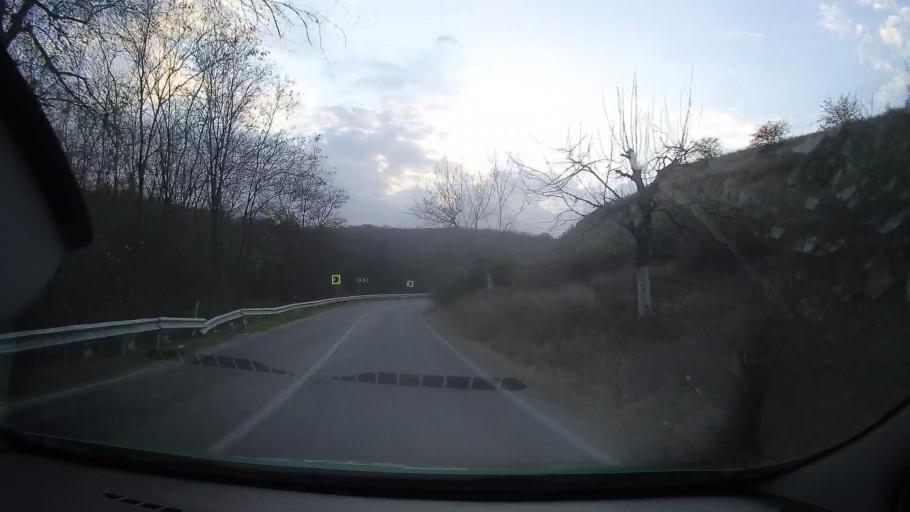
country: RO
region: Constanta
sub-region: Comuna Baneasa
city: Baneasa
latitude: 44.0766
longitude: 27.6713
